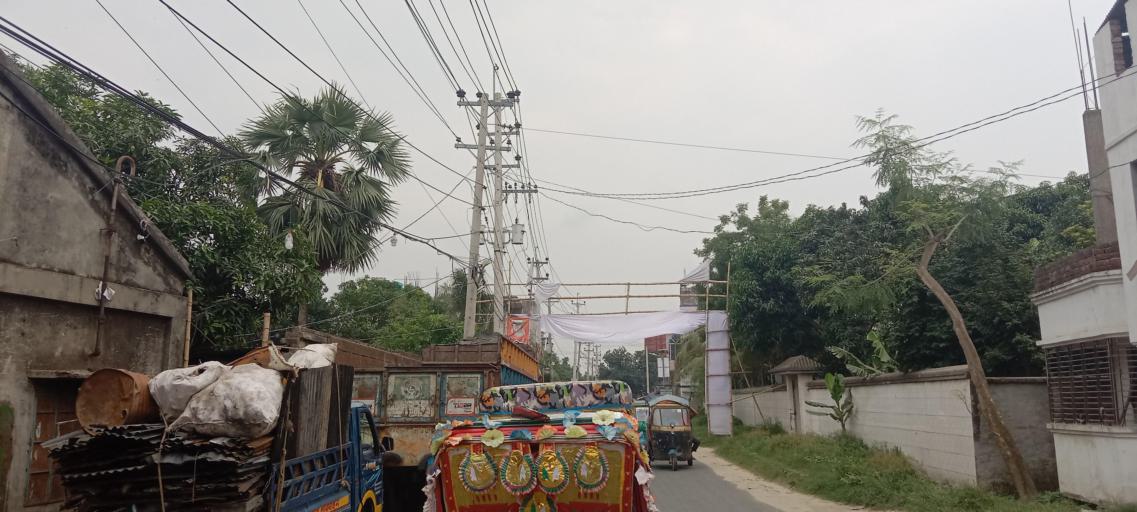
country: BD
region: Dhaka
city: Azimpur
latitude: 23.7097
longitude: 90.3469
